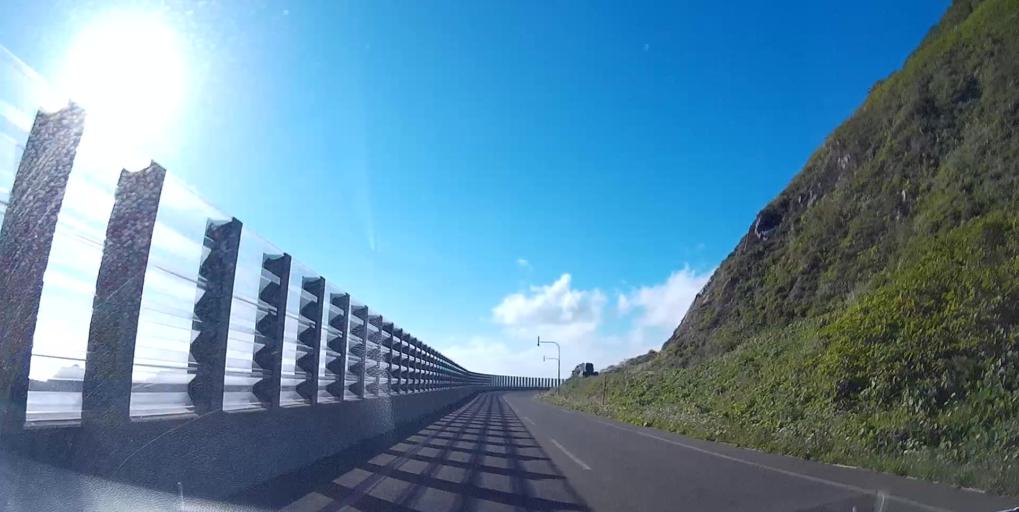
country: JP
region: Hokkaido
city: Iwanai
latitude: 42.3271
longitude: 139.7741
